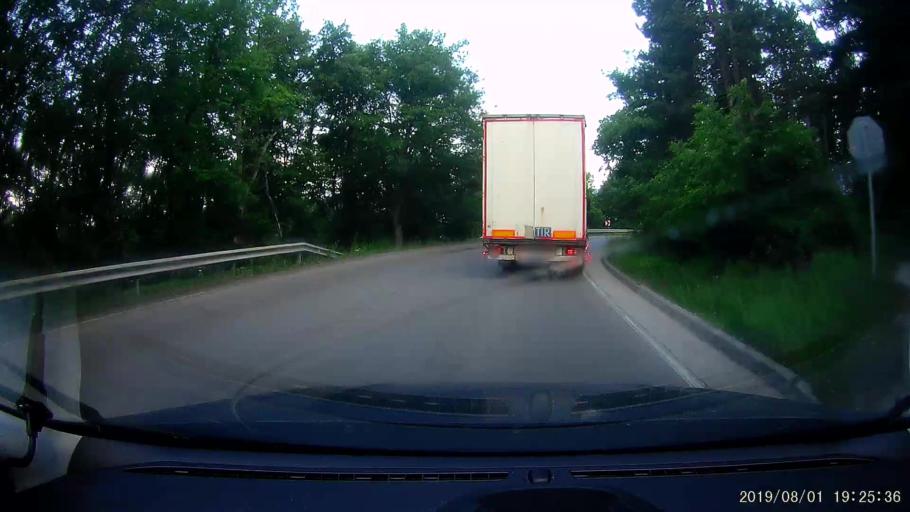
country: BG
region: Burgas
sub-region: Obshtina Sungurlare
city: Sungurlare
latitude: 42.8594
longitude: 26.9463
